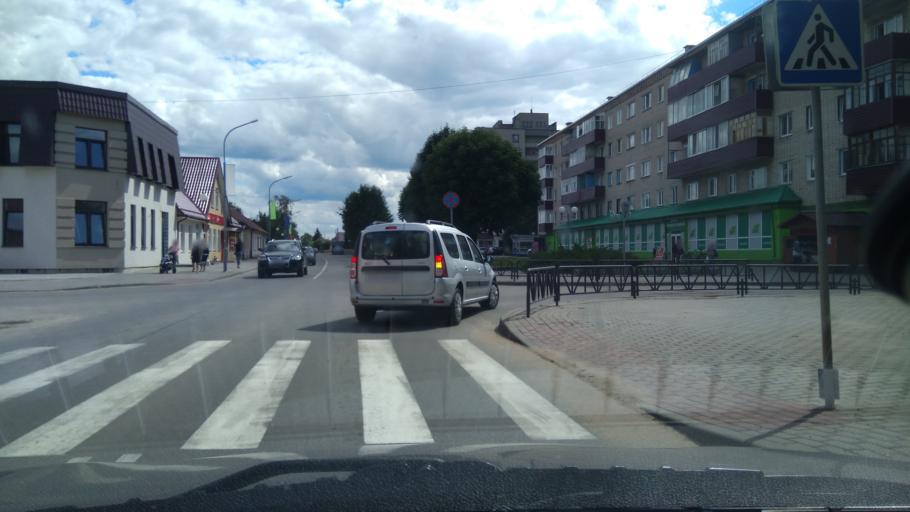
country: BY
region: Grodnenskaya
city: Shchuchin
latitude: 53.6031
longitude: 24.7420
